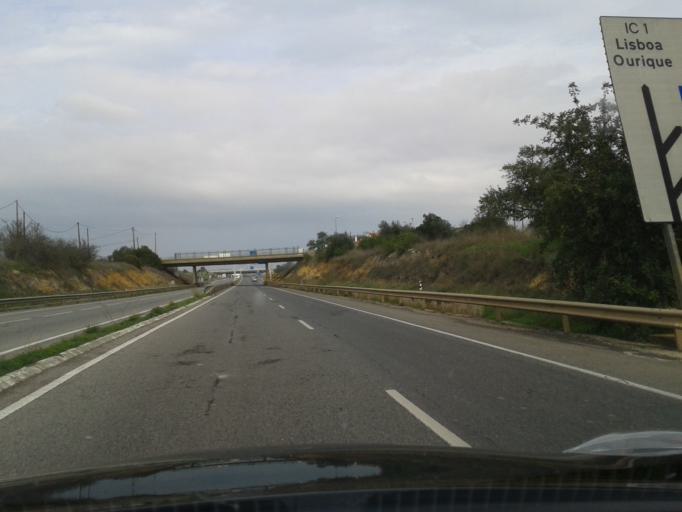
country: PT
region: Faro
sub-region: Albufeira
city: Ferreiras
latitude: 37.1303
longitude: -8.2573
